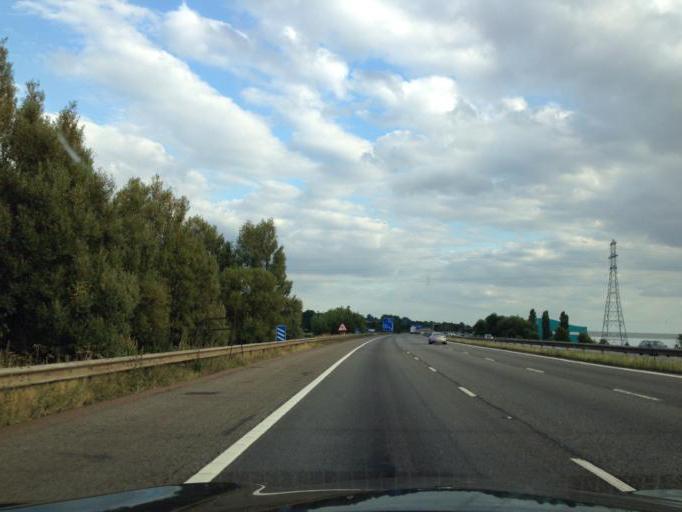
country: GB
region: England
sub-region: Oxfordshire
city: Banbury
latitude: 52.0809
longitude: -1.3205
